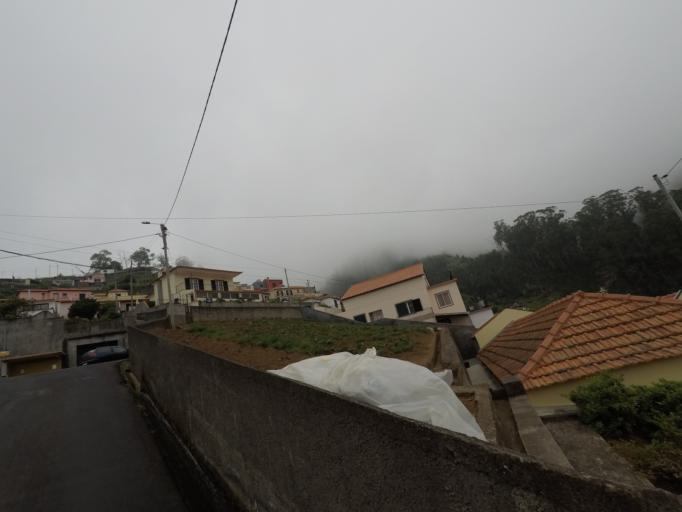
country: PT
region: Madeira
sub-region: Camara de Lobos
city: Curral das Freiras
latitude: 32.6855
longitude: -16.9470
